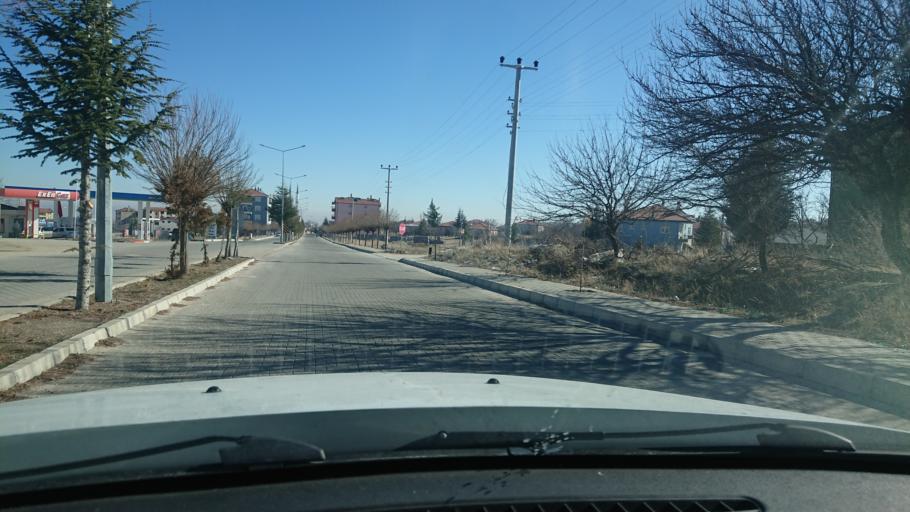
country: TR
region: Aksaray
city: Agacoren
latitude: 38.8692
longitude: 33.9102
